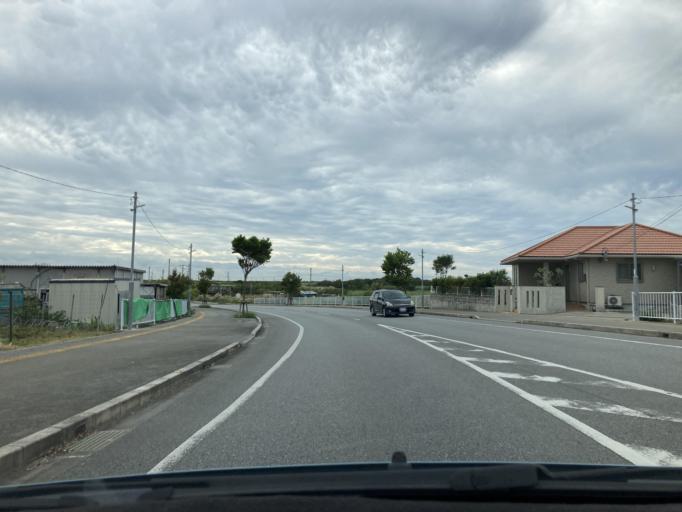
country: JP
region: Okinawa
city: Ishikawa
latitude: 26.4020
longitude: 127.7391
